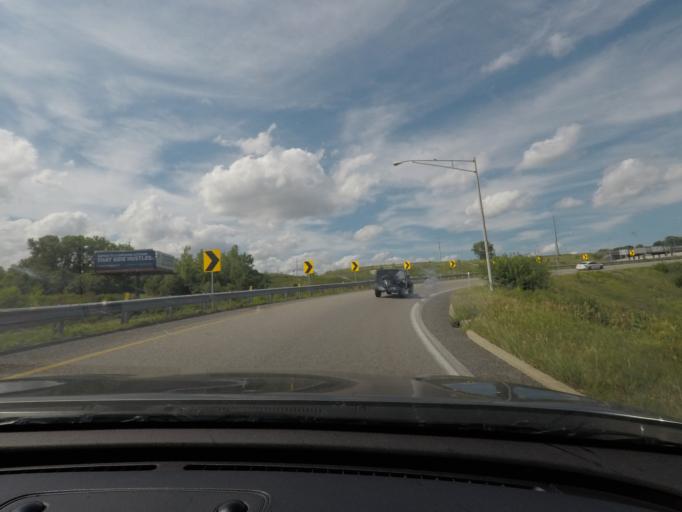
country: US
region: Missouri
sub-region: Jackson County
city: Raytown
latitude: 39.0607
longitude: -94.4910
